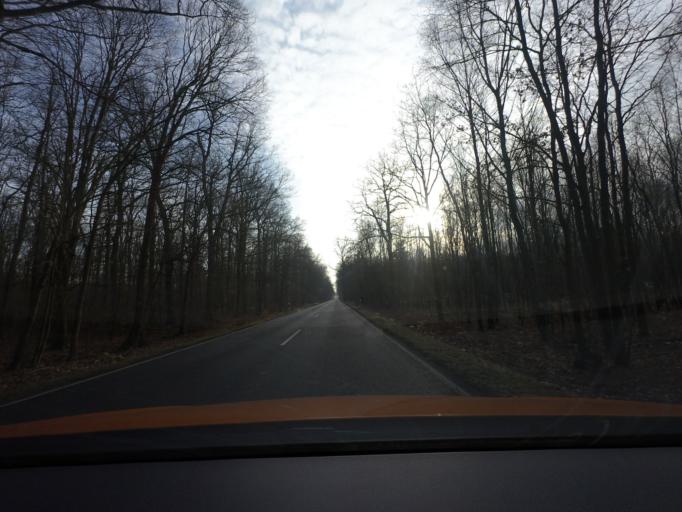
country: DE
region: Brandenburg
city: Liebenwalde
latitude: 52.8113
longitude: 13.4062
